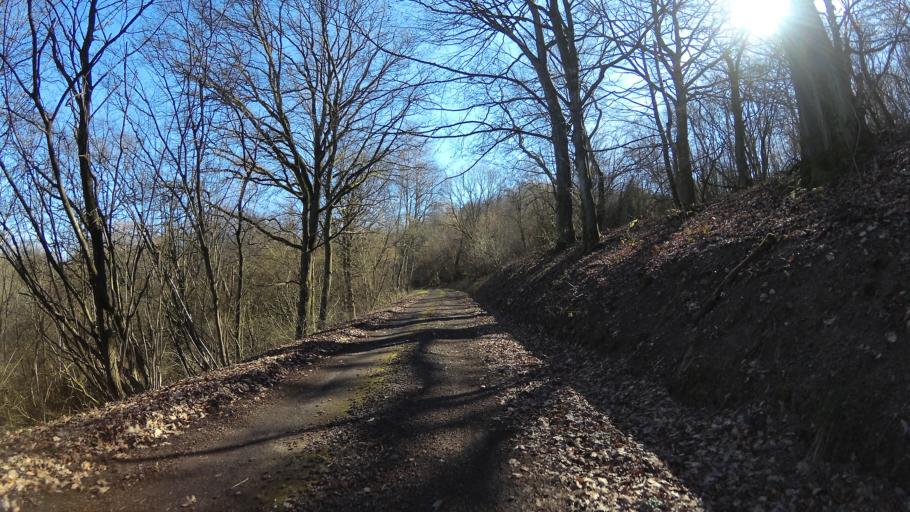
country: DE
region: Rheinland-Pfalz
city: Breitenbach
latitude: 49.4577
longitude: 7.2488
